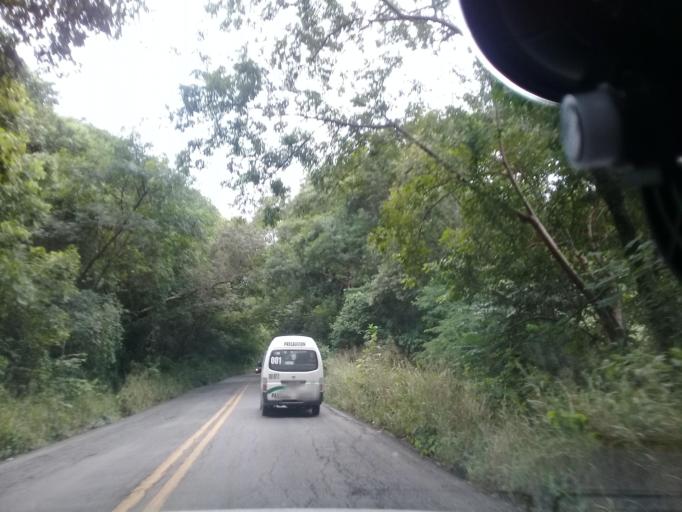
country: MX
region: Hidalgo
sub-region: Huejutla de Reyes
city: Parque de Poblamiento Solidaridad
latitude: 21.1981
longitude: -98.3891
